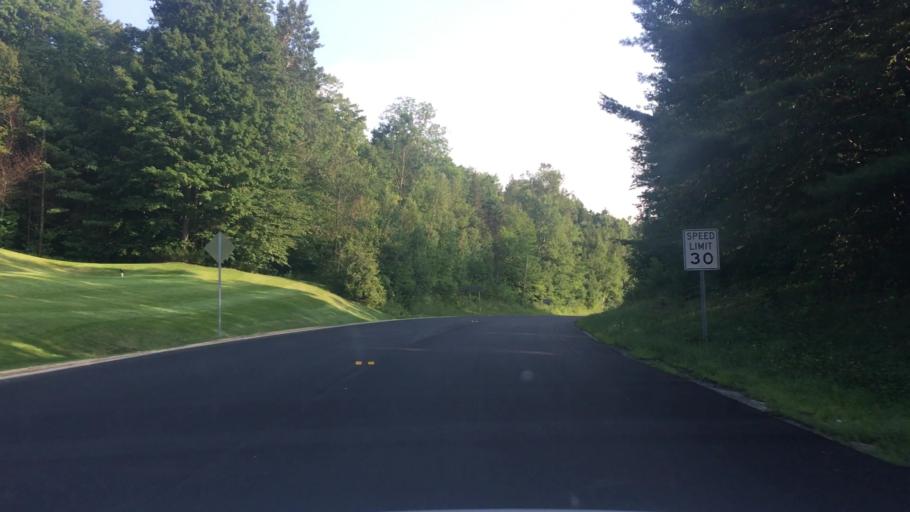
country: US
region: New Hampshire
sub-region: Sullivan County
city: Grantham
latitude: 43.5019
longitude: -72.1307
